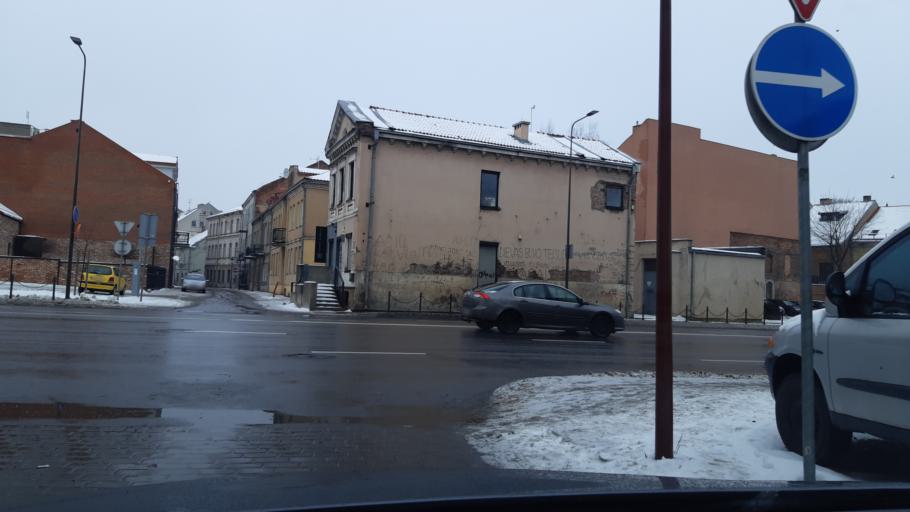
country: LT
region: Kauno apskritis
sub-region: Kaunas
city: Kaunas
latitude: 54.8957
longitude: 23.8964
